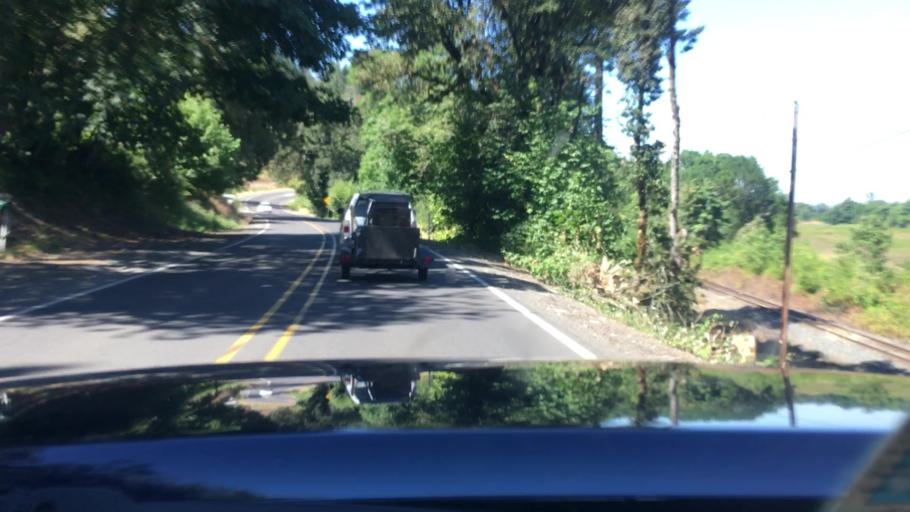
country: US
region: Oregon
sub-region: Lane County
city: Cottage Grove
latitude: 43.8192
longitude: -123.0462
